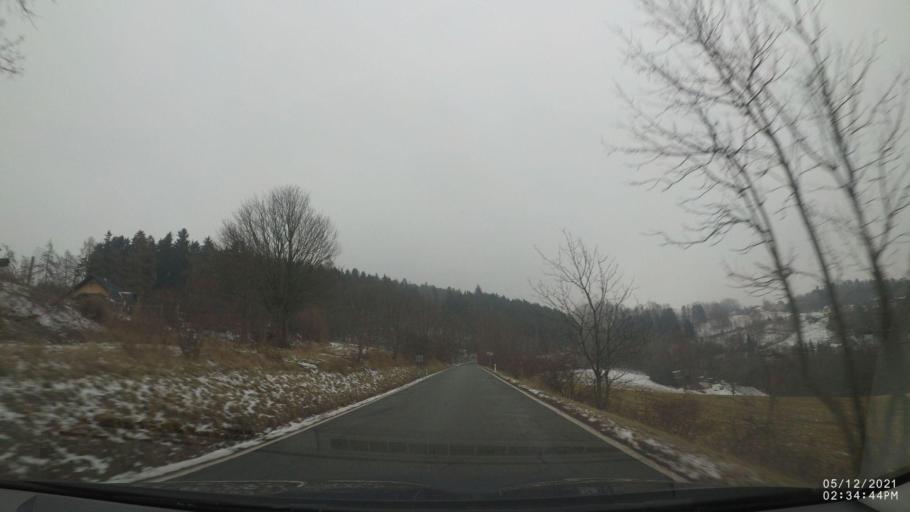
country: CZ
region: Kralovehradecky
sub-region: Okres Nachod
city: Nachod
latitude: 50.4033
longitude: 16.1672
